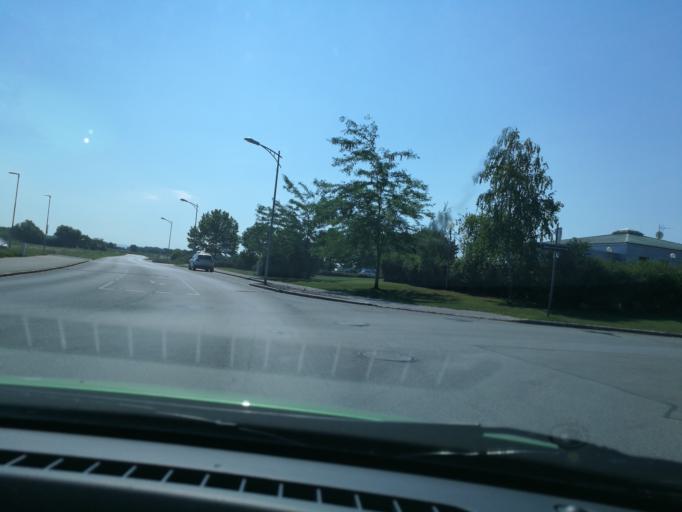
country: AT
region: Lower Austria
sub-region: Politischer Bezirk Ganserndorf
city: Ganserndorf
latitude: 48.3465
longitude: 16.7282
